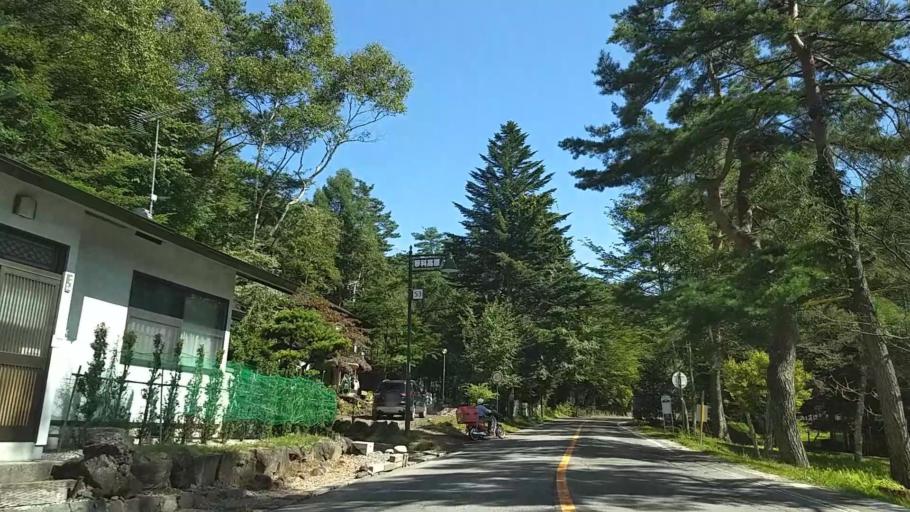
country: JP
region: Nagano
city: Chino
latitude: 36.0599
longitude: 138.2685
